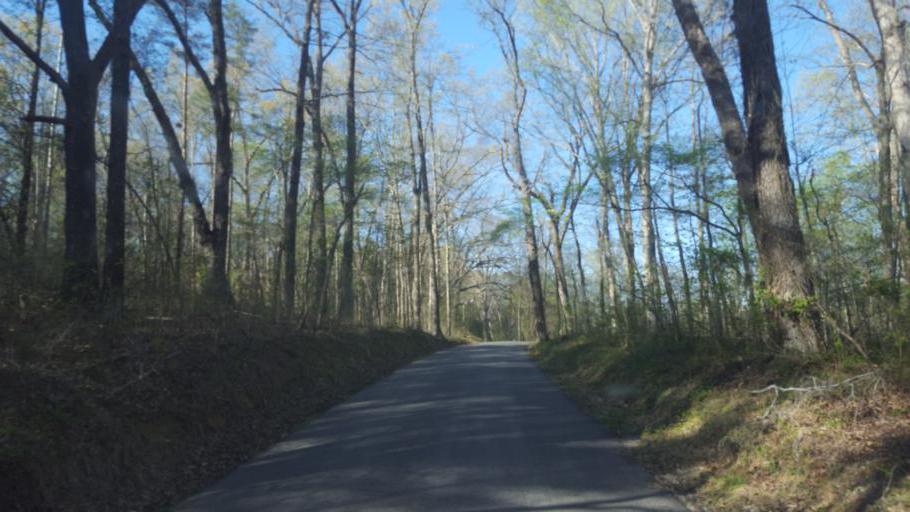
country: US
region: Kentucky
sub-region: Barren County
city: Cave City
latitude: 37.1888
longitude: -86.0493
